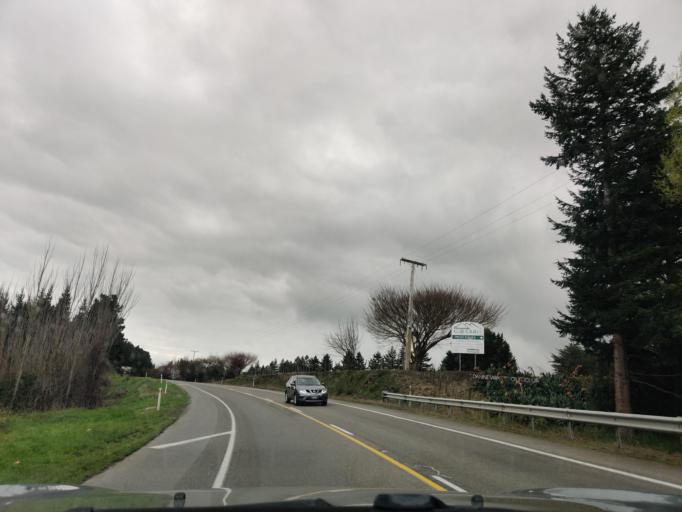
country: NZ
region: Manawatu-Wanganui
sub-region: Palmerston North City
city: Palmerston North
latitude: -40.2287
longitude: 176.0666
